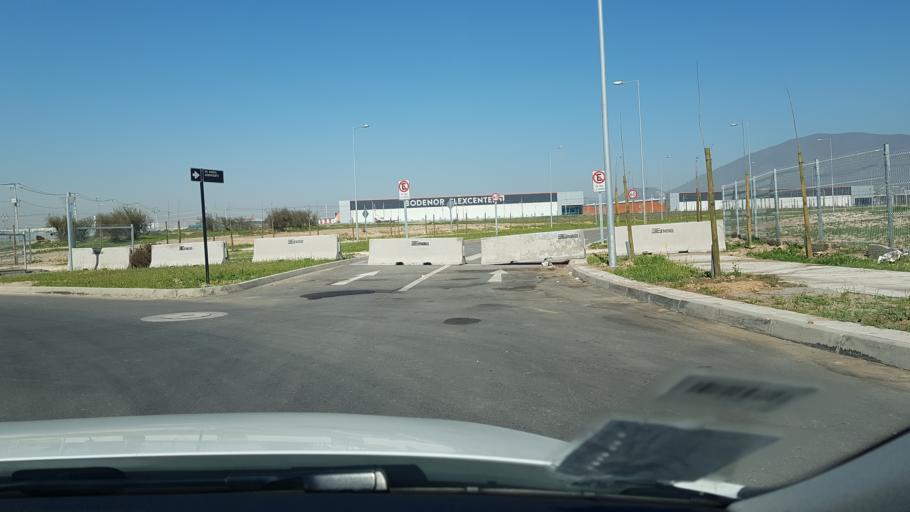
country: CL
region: Santiago Metropolitan
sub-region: Provincia de Santiago
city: Lo Prado
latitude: -33.4232
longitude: -70.7897
